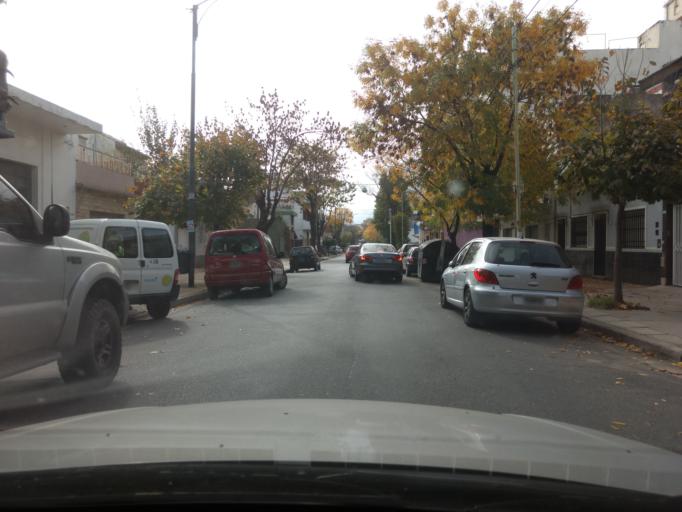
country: AR
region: Buenos Aires F.D.
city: Villa Santa Rita
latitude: -34.6222
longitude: -58.5114
